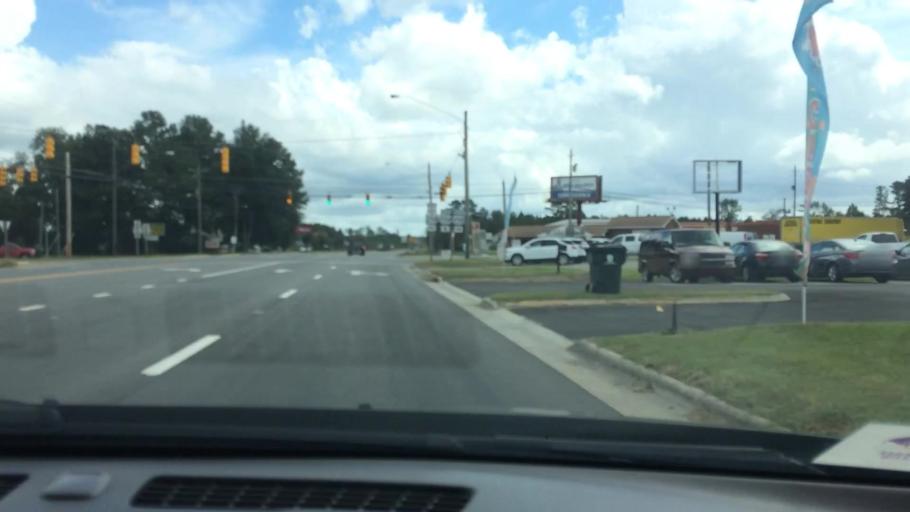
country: US
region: North Carolina
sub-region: Pitt County
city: Farmville
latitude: 35.5818
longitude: -77.5940
